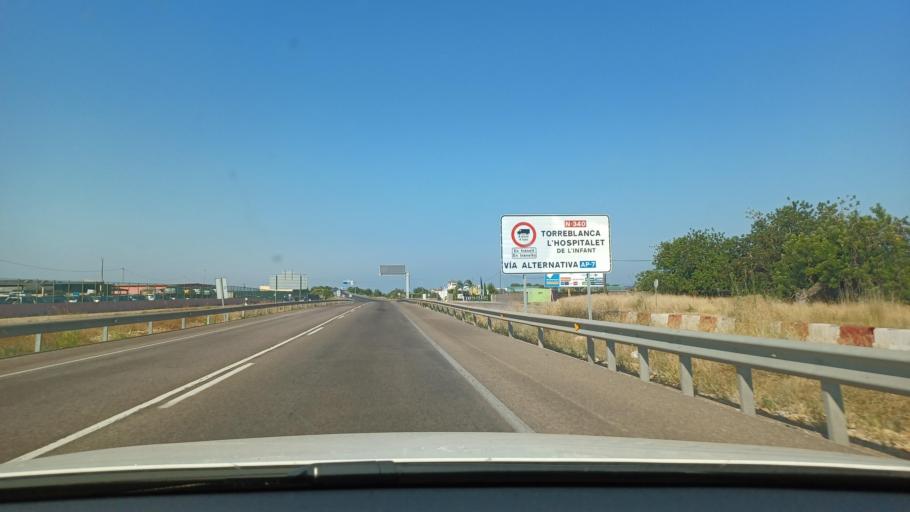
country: ES
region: Valencia
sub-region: Provincia de Castello
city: Peniscola
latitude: 40.3978
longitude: 0.3647
